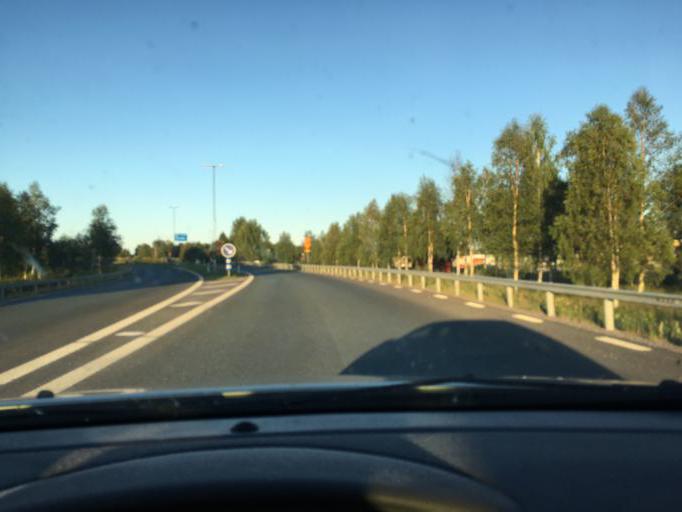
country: SE
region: Norrbotten
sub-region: Kalix Kommun
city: Rolfs
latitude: 65.8512
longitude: 23.1181
